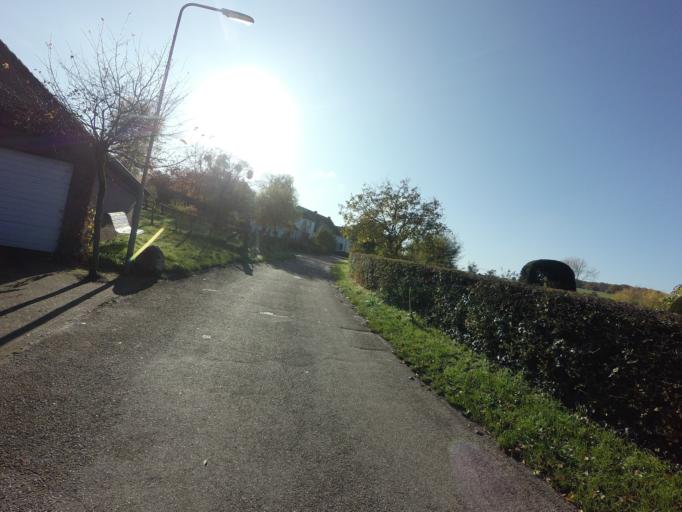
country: NL
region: Limburg
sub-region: Eijsden-Margraten
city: Margraten
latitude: 50.7987
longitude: 5.8690
